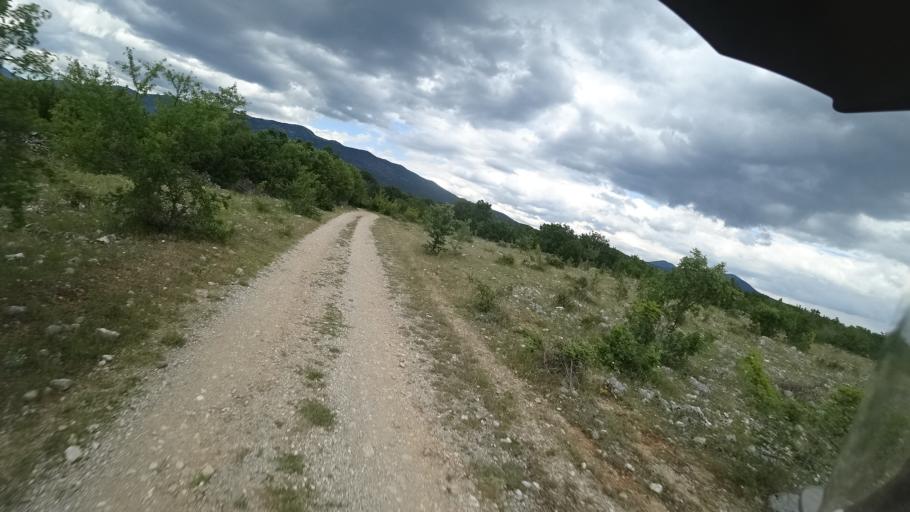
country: HR
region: Zadarska
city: Gracac
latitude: 44.1521
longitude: 15.9311
